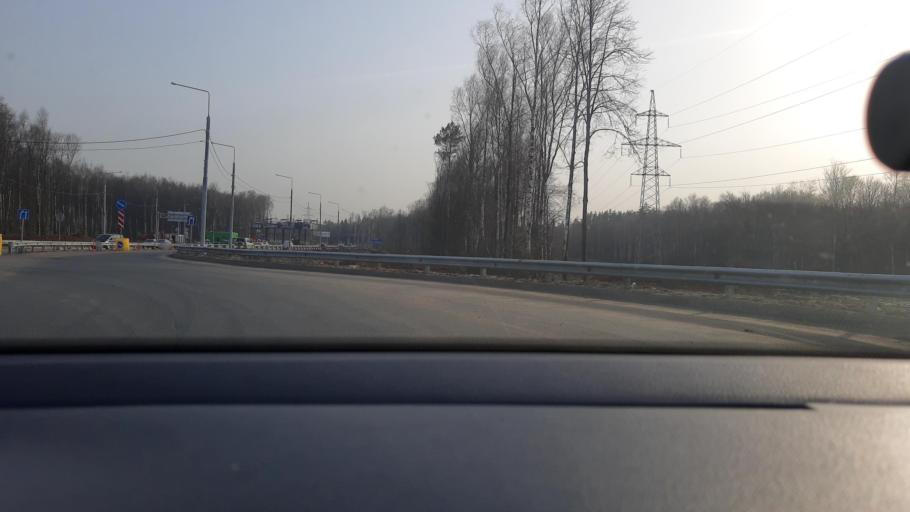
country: RU
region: Moskovskaya
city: Barvikha
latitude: 55.7209
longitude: 37.3160
